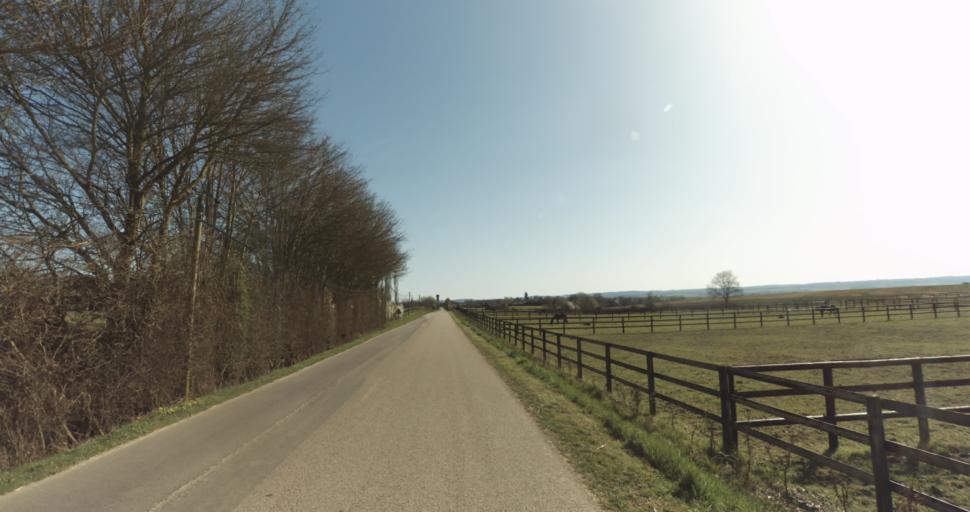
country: FR
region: Lower Normandy
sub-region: Departement de l'Orne
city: Trun
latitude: 48.8802
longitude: 0.0288
